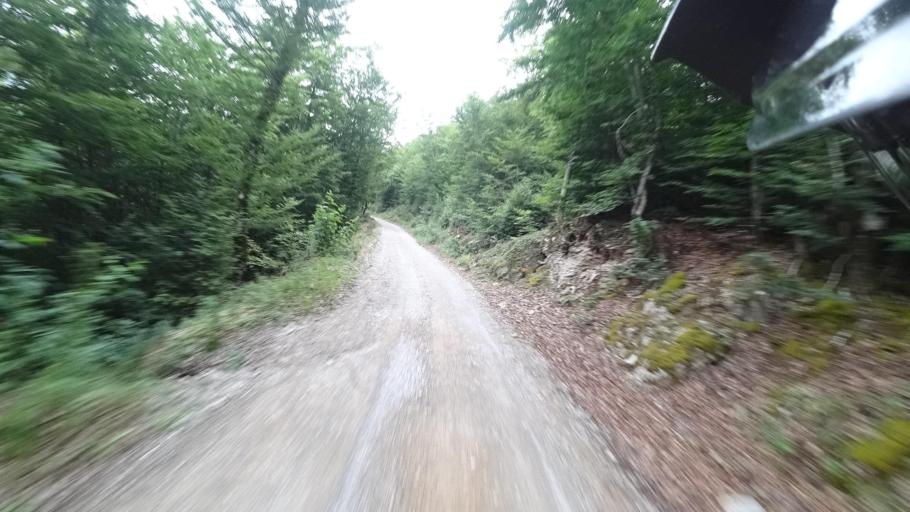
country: HR
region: Zadarska
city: Gracac
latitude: 44.5158
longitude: 15.8626
